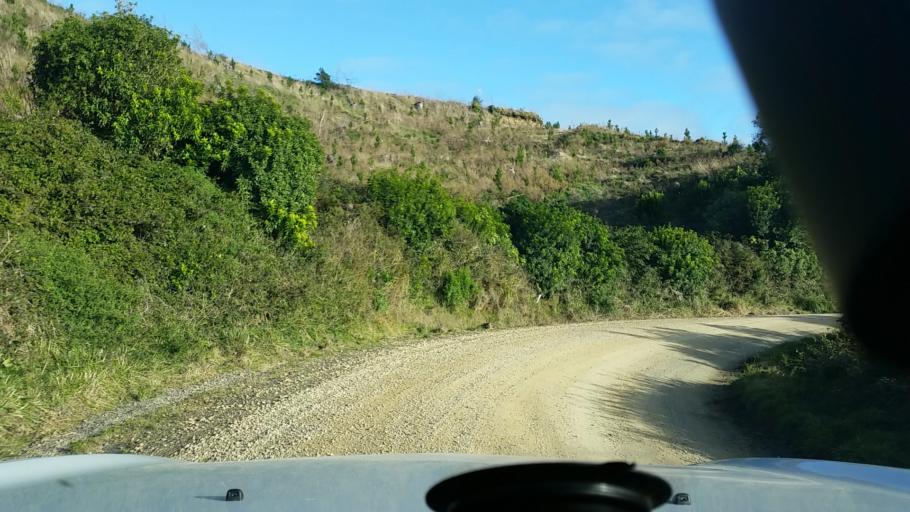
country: NZ
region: Hawke's Bay
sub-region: Napier City
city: Napier
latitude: -39.2605
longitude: 176.8488
